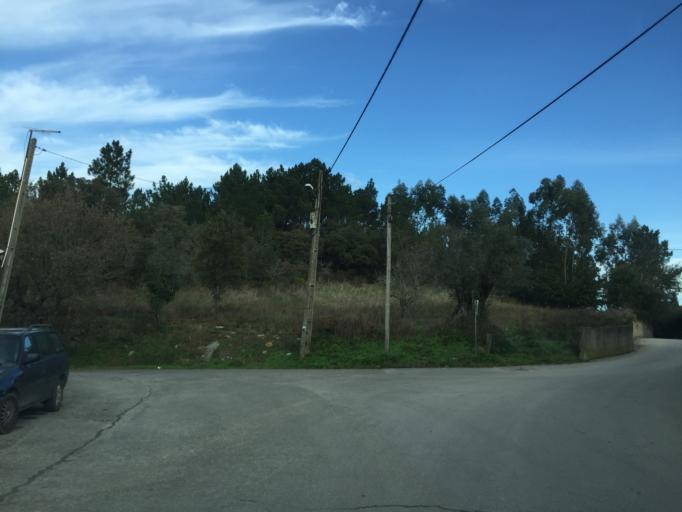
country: PT
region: Lisbon
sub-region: Odivelas
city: Canecas
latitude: 38.8188
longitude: -9.2475
